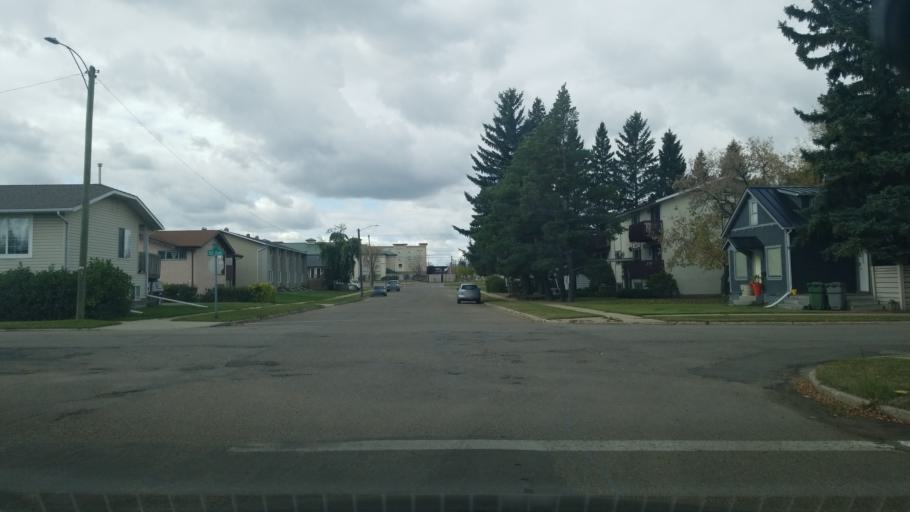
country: CA
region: Saskatchewan
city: Lloydminster
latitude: 53.2790
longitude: -110.0176
